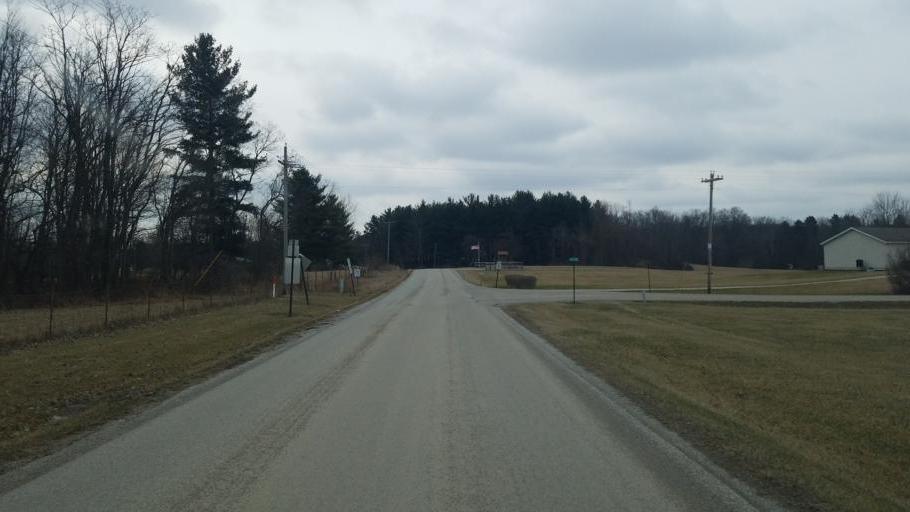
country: US
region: Ohio
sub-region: Morrow County
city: Mount Gilead
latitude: 40.6109
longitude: -82.7853
